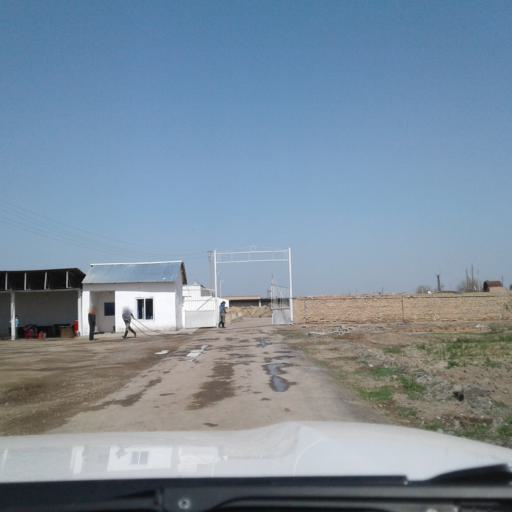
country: TM
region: Lebap
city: Turkmenabat
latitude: 38.9600
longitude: 63.6455
